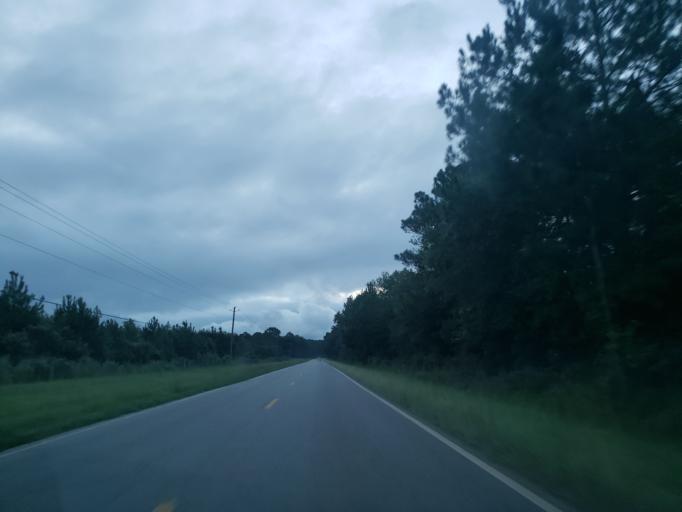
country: US
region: Georgia
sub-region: Chatham County
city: Bloomingdale
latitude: 32.0548
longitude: -81.2963
